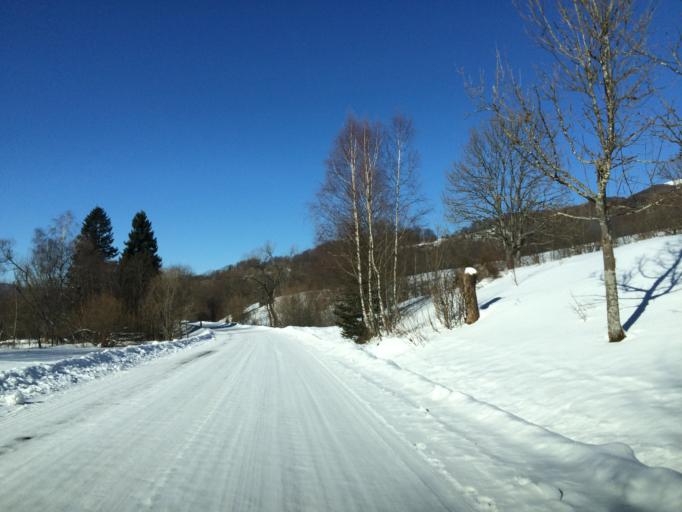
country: PL
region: Subcarpathian Voivodeship
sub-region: Powiat bieszczadzki
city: Lutowiska
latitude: 49.1454
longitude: 22.5267
